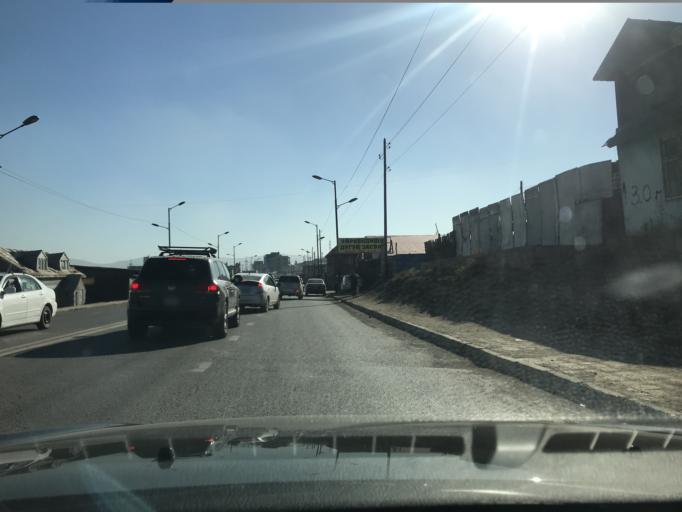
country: MN
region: Ulaanbaatar
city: Ulaanbaatar
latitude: 47.9735
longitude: 106.9178
